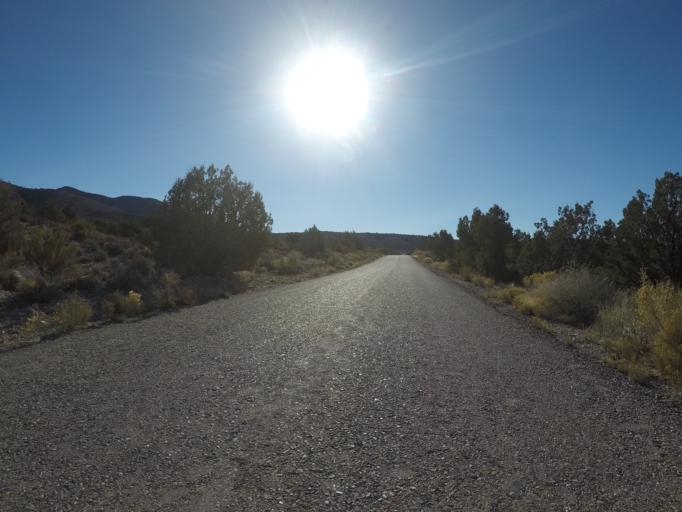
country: US
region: Nevada
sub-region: Clark County
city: Summerlin South
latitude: 36.0941
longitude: -115.5646
